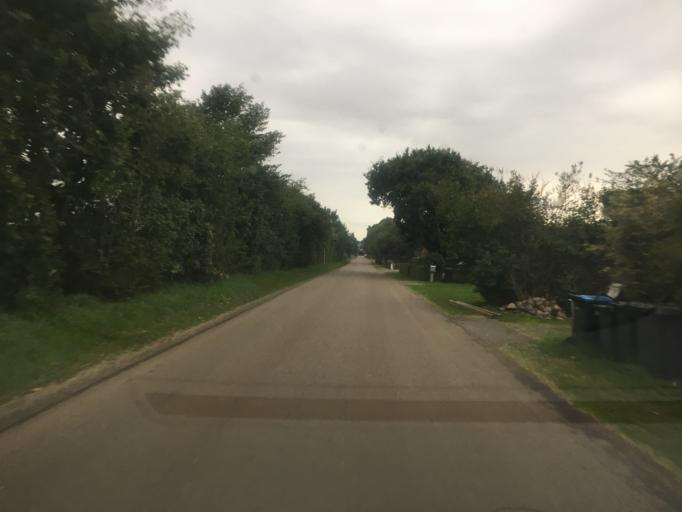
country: DE
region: Schleswig-Holstein
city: Ellhoft
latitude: 54.9495
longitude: 8.9730
